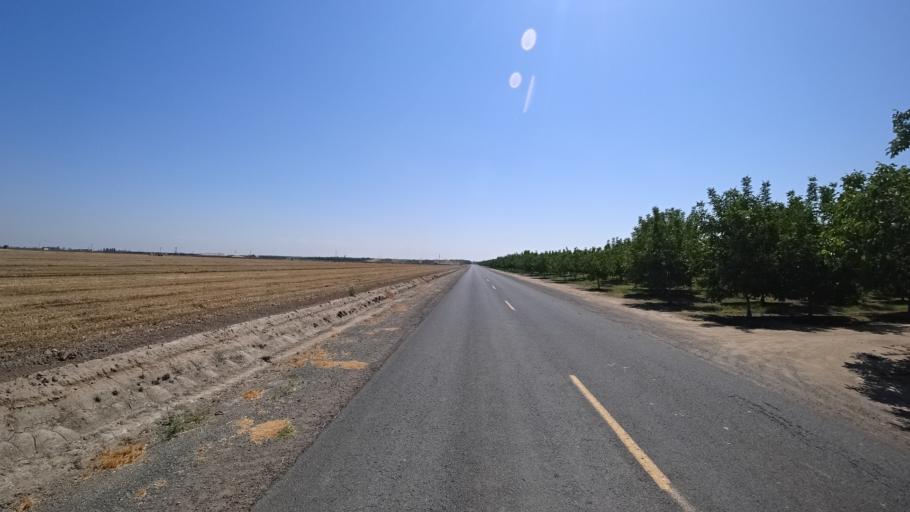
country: US
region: California
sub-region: Kings County
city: Lucerne
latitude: 36.3717
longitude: -119.7044
